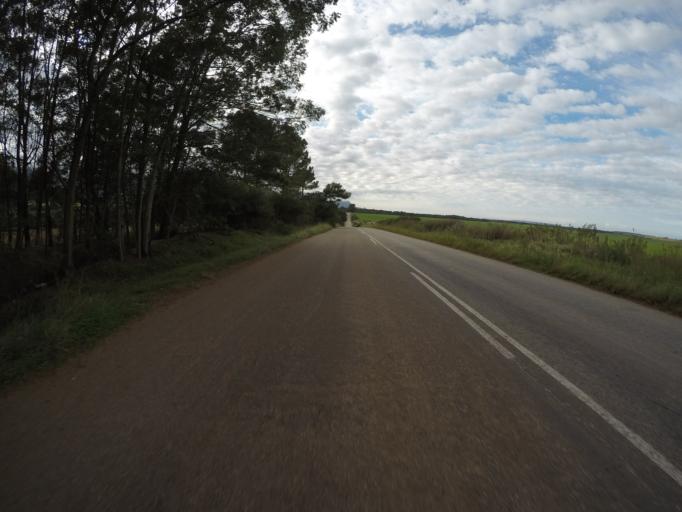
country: ZA
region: Eastern Cape
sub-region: Cacadu District Municipality
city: Kareedouw
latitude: -34.0110
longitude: 24.2850
